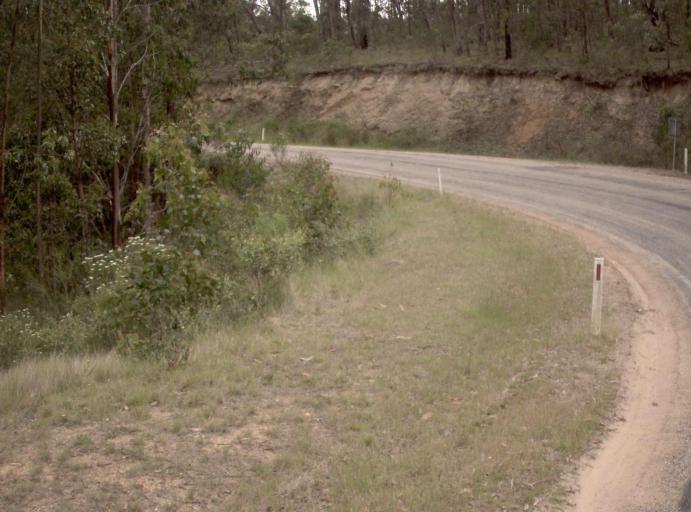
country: AU
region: Victoria
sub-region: East Gippsland
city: Bairnsdale
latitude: -37.5966
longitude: 147.1939
